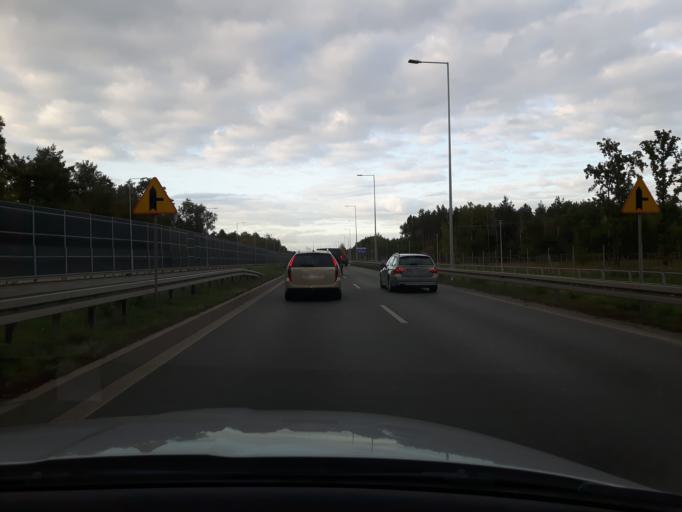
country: PL
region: Masovian Voivodeship
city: Zielonka
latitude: 52.2866
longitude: 21.1401
